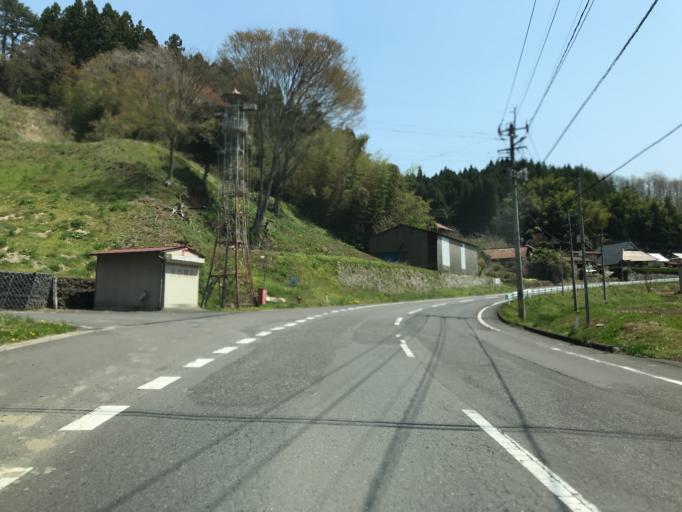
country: JP
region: Fukushima
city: Ishikawa
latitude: 37.0649
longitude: 140.4479
